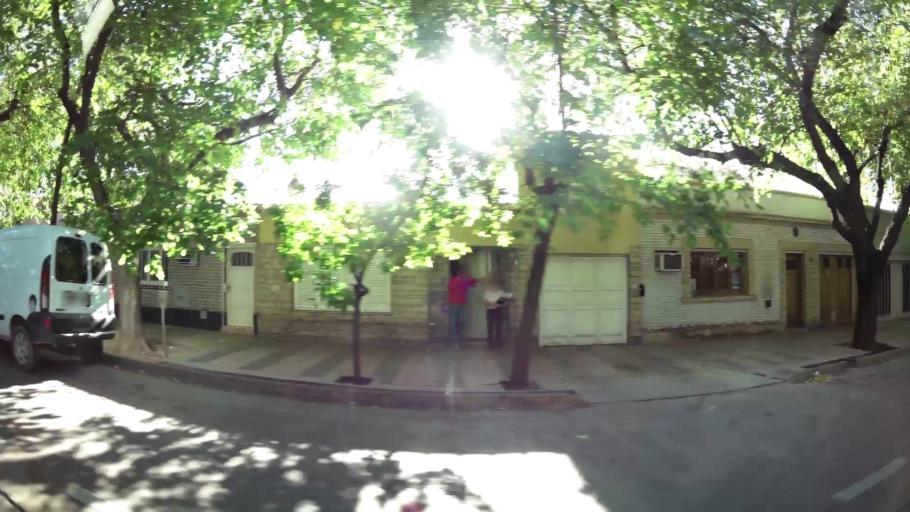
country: AR
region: Mendoza
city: Mendoza
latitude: -32.8991
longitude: -68.8374
